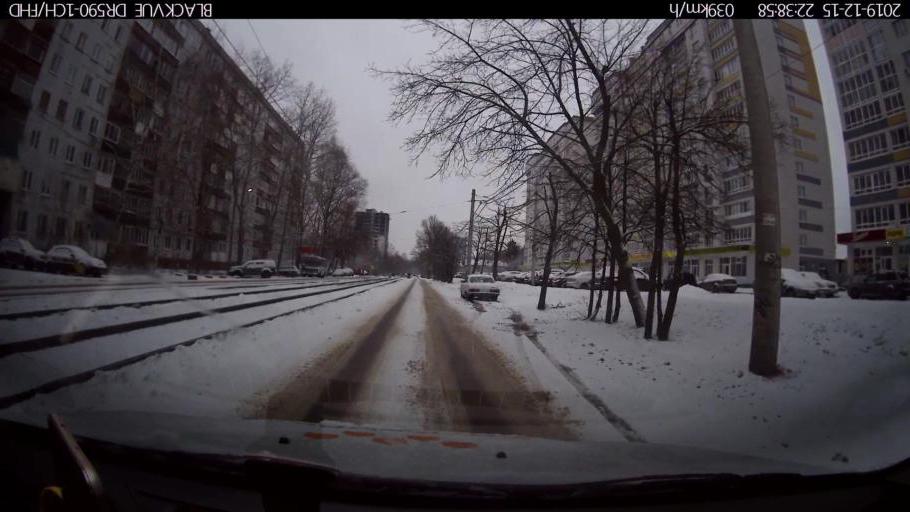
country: RU
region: Nizjnij Novgorod
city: Gorbatovka
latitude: 56.3418
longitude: 43.8379
